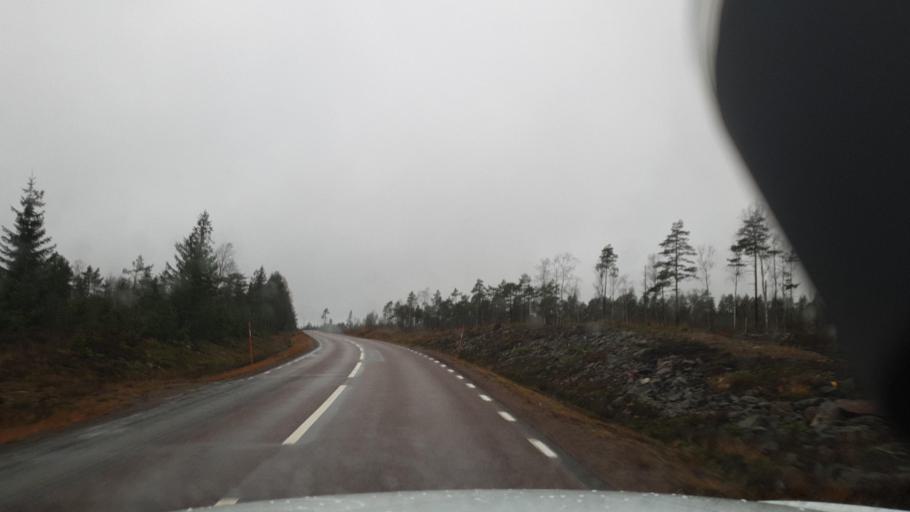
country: SE
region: Vaermland
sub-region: Sunne Kommun
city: Sunne
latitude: 59.6922
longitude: 13.0714
